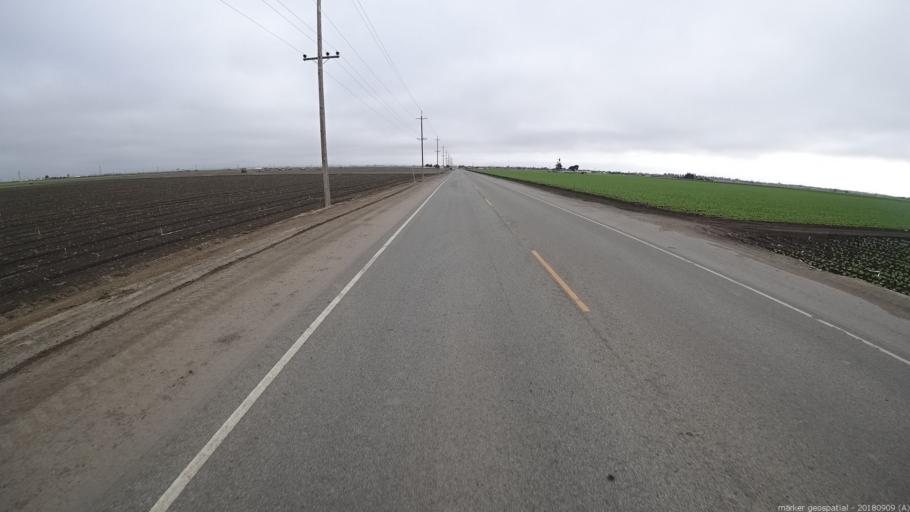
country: US
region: California
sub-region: Monterey County
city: Salinas
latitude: 36.6536
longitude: -121.6963
